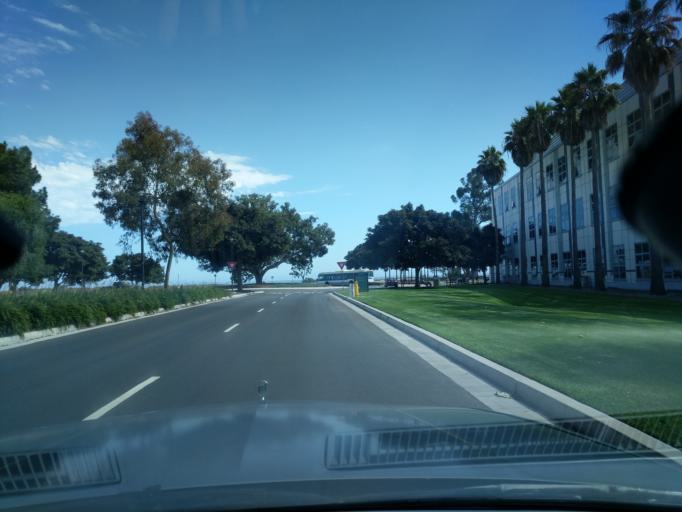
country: US
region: California
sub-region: Santa Barbara County
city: Isla Vista
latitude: 34.4157
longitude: -119.8397
